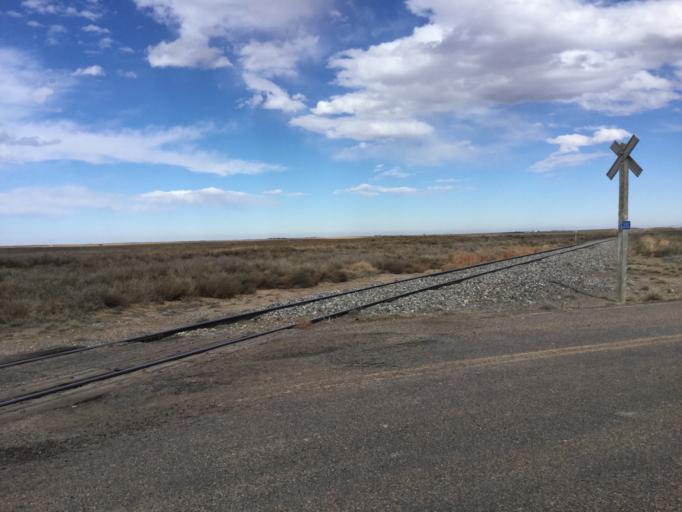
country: US
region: Kansas
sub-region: Morton County
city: Elkhart
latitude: 37.0396
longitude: -101.8422
